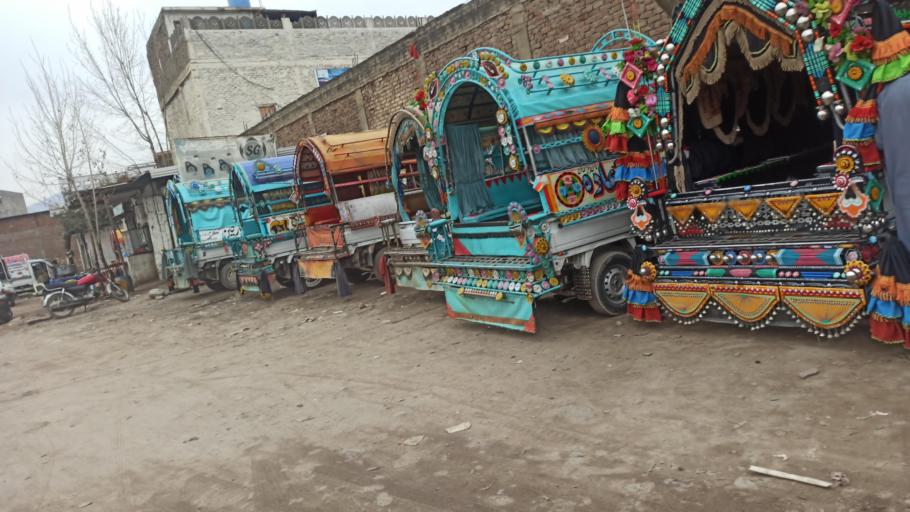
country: PK
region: Khyber Pakhtunkhwa
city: Mingora
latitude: 34.7727
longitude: 72.3527
